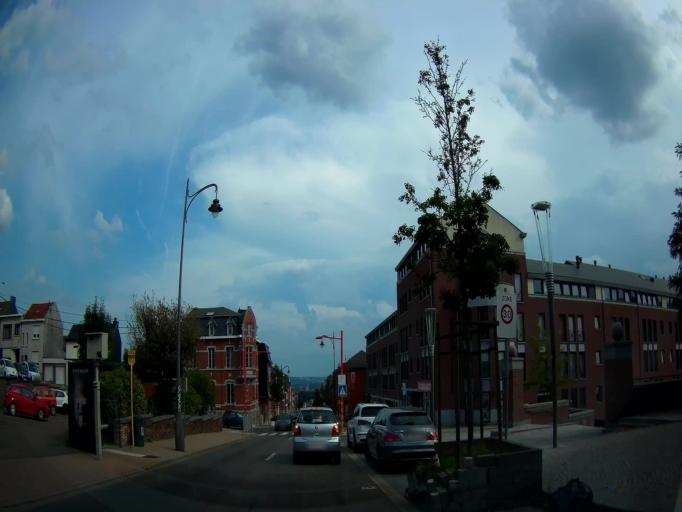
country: BE
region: Wallonia
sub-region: Province de Liege
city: Ans
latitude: 50.6541
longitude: 5.5356
